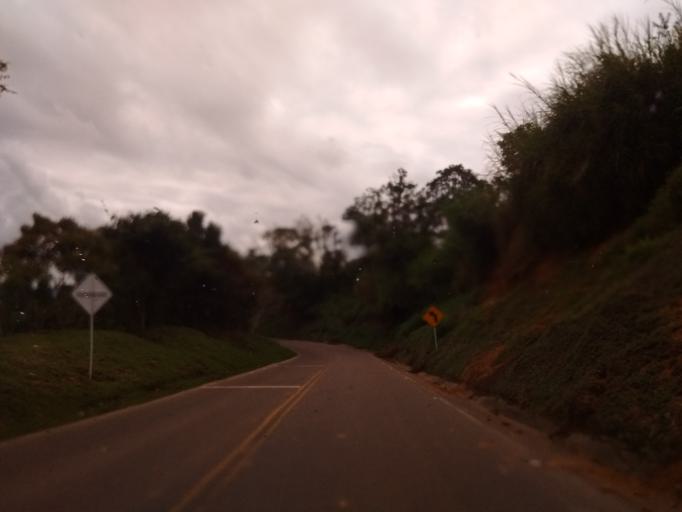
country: CO
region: Huila
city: Isnos
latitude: 1.9217
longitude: -76.2196
